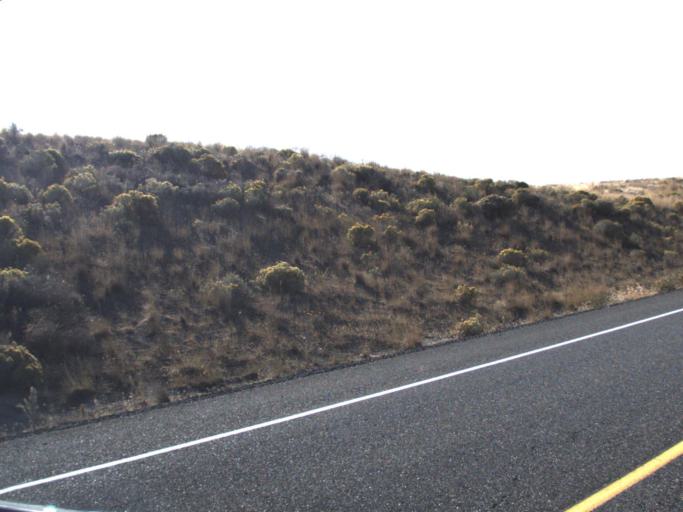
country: US
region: Washington
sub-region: Benton County
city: Highland
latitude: 46.1505
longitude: -119.1283
